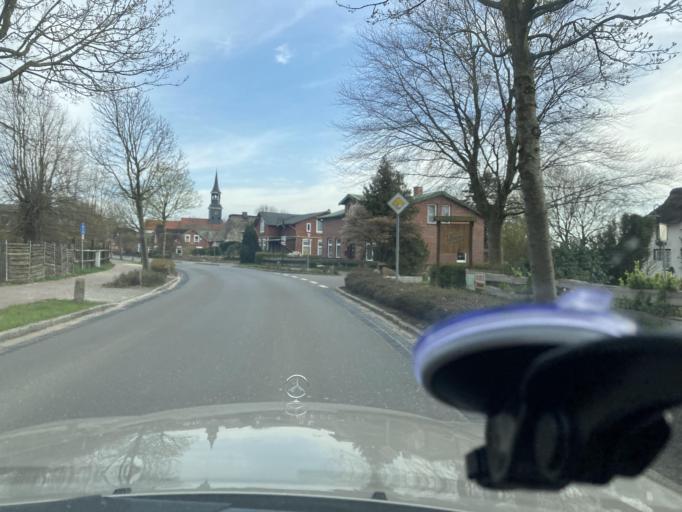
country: DE
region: Schleswig-Holstein
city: Lehe
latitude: 54.3365
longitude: 9.0224
